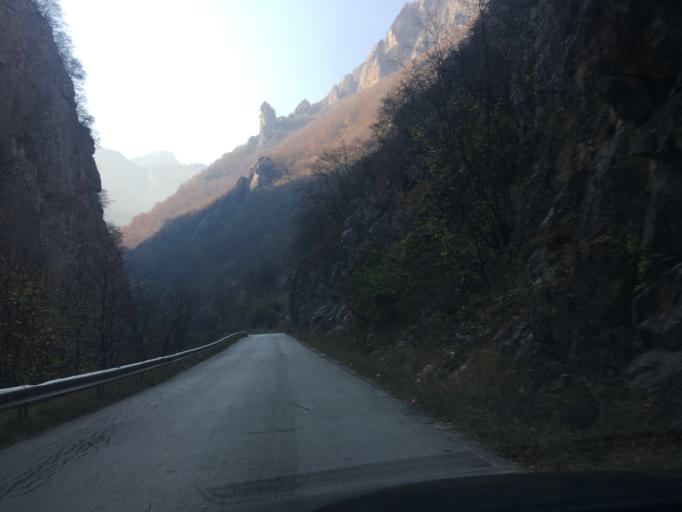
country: XK
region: Pec
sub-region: Komuna e Pejes
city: Peje
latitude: 42.6656
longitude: 20.2279
